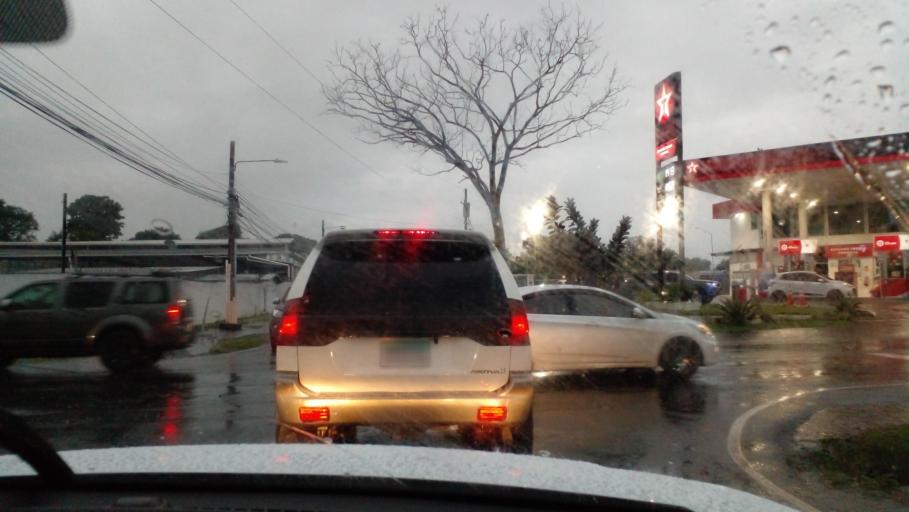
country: PA
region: Chiriqui
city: Mata del Nance
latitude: 8.4473
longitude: -82.4217
